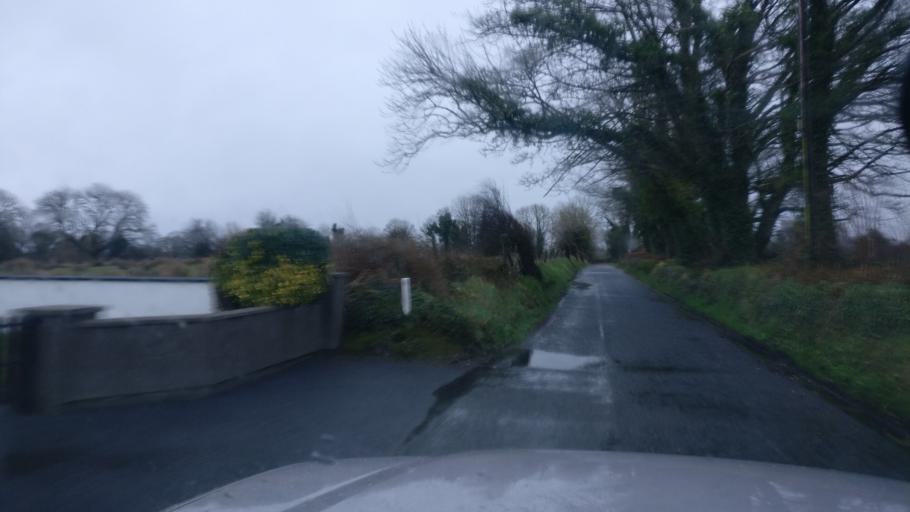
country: IE
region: Connaught
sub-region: County Galway
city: Ballinasloe
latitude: 53.3281
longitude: -8.3918
